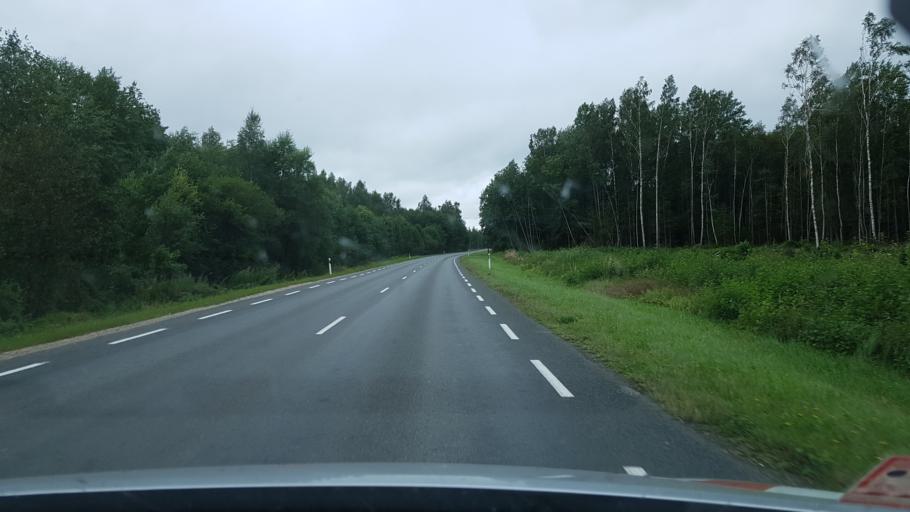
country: EE
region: Viljandimaa
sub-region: Viiratsi vald
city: Viiratsi
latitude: 58.4378
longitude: 25.7299
